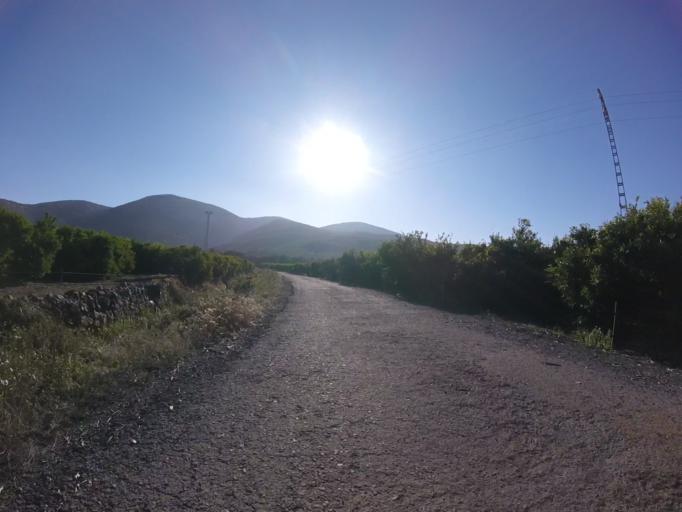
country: ES
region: Valencia
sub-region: Provincia de Castello
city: Santa Magdalena de Pulpis
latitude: 40.3794
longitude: 0.3377
